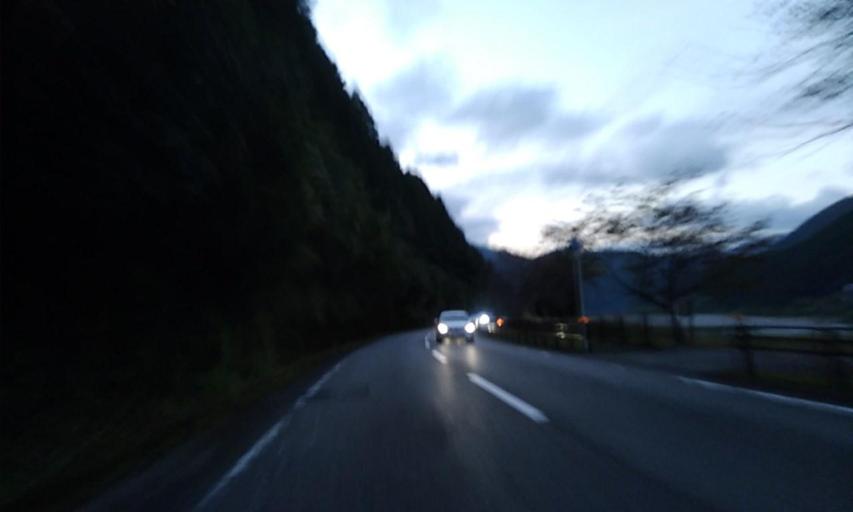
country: JP
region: Wakayama
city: Shingu
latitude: 33.7273
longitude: 135.9519
